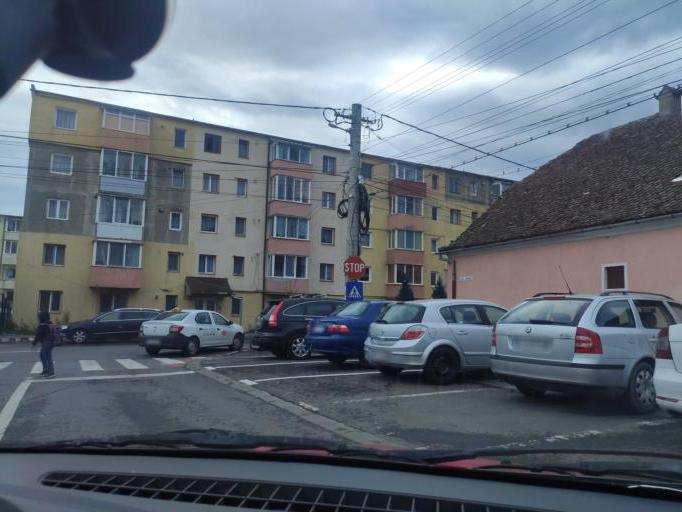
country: RO
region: Brasov
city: Codlea
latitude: 45.7040
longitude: 25.4476
